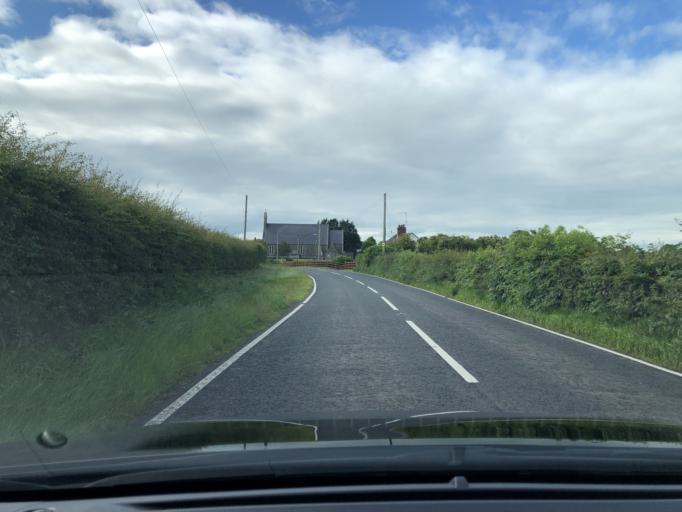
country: GB
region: Northern Ireland
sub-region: Down District
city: Dundrum
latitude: 54.2688
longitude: -5.7851
